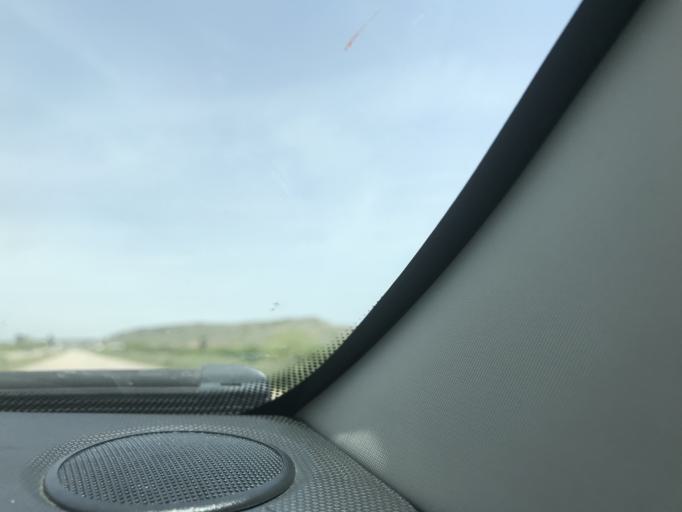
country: TR
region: Osmaniye
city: Toprakkale
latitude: 37.0114
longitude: 36.1375
